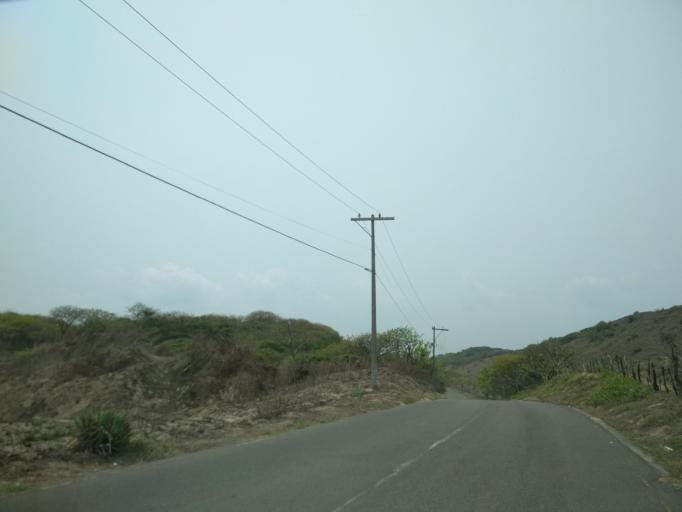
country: MX
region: Veracruz
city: Anton Lizardo
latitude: 19.0473
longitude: -96.0306
